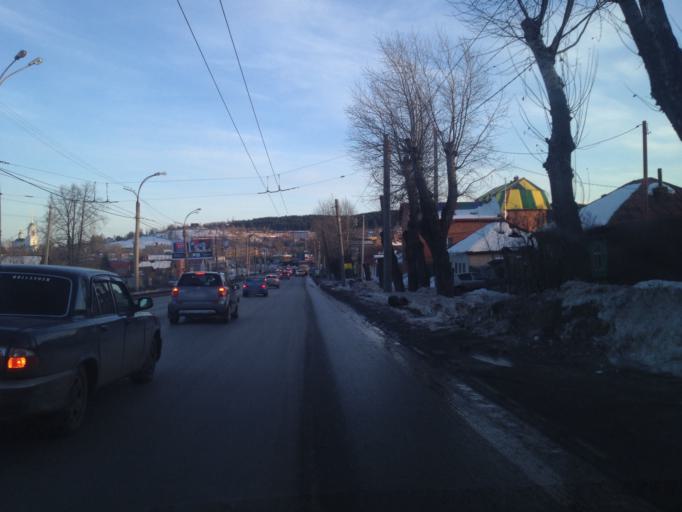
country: RU
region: Sverdlovsk
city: Istok
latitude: 56.7509
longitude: 60.6789
